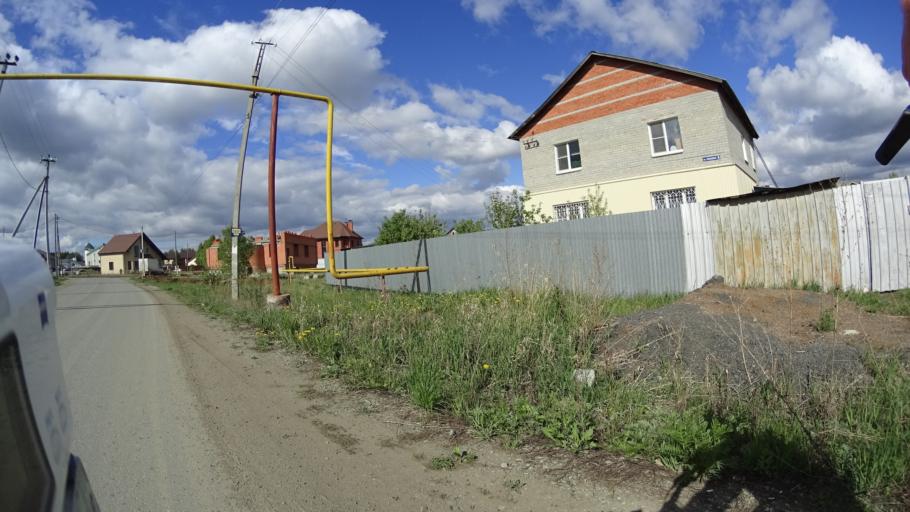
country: RU
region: Chelyabinsk
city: Sargazy
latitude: 55.1534
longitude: 61.2399
